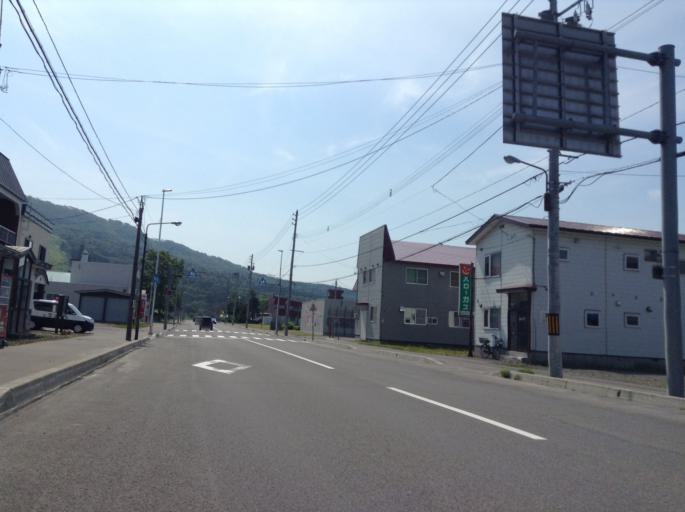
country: JP
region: Hokkaido
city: Nayoro
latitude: 44.7270
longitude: 142.2604
